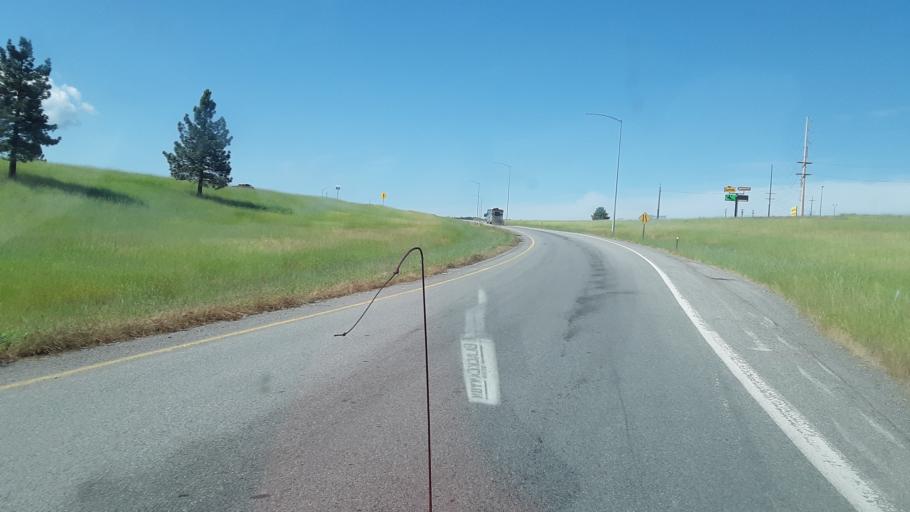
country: US
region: Idaho
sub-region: Kootenai County
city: Post Falls
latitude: 47.7101
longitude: -117.0022
